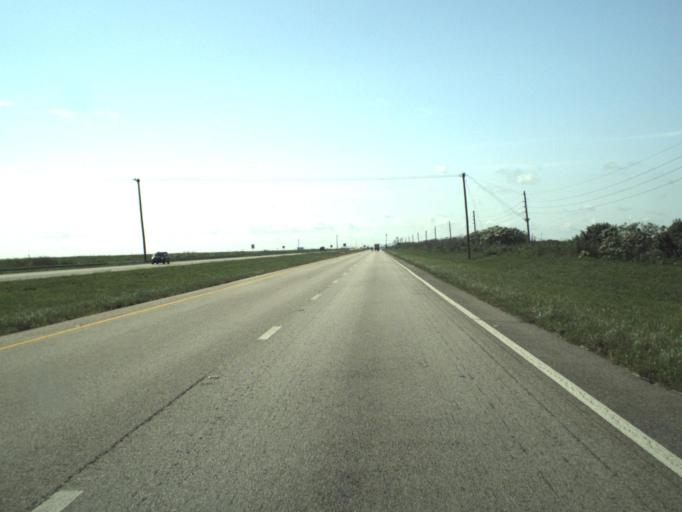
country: US
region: Florida
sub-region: Palm Beach County
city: Belle Glade Camp
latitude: 26.4068
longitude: -80.5936
